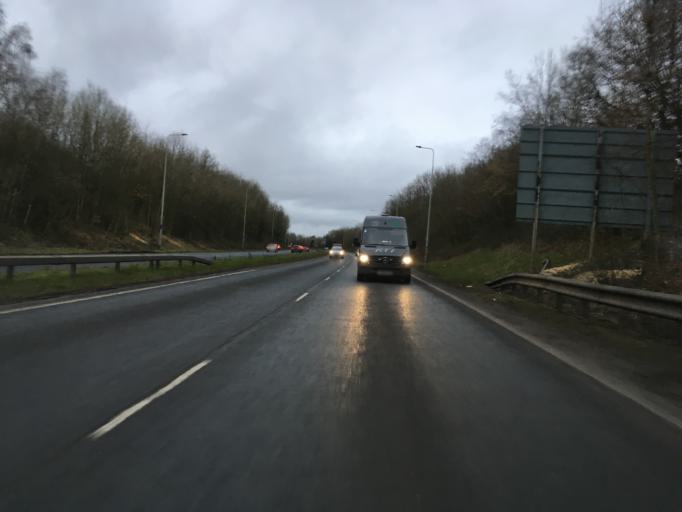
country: GB
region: Wales
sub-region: Rhondda Cynon Taf
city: Llantrisant
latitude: 51.5143
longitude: -3.3573
